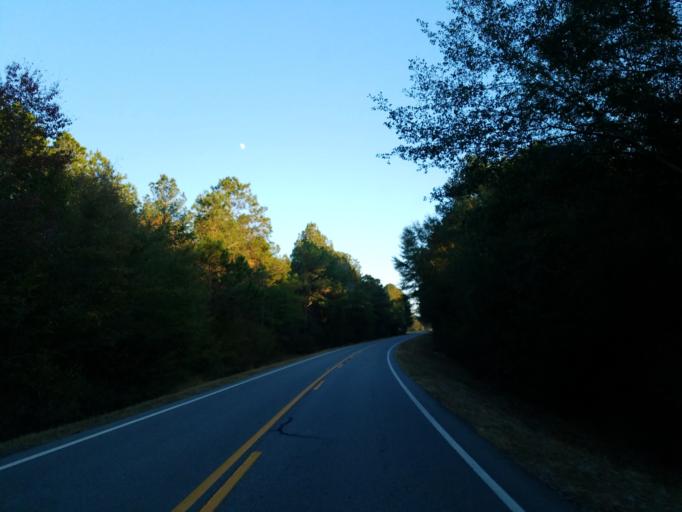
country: US
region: Georgia
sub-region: Wilcox County
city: Rochelle
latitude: 31.8130
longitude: -83.4996
